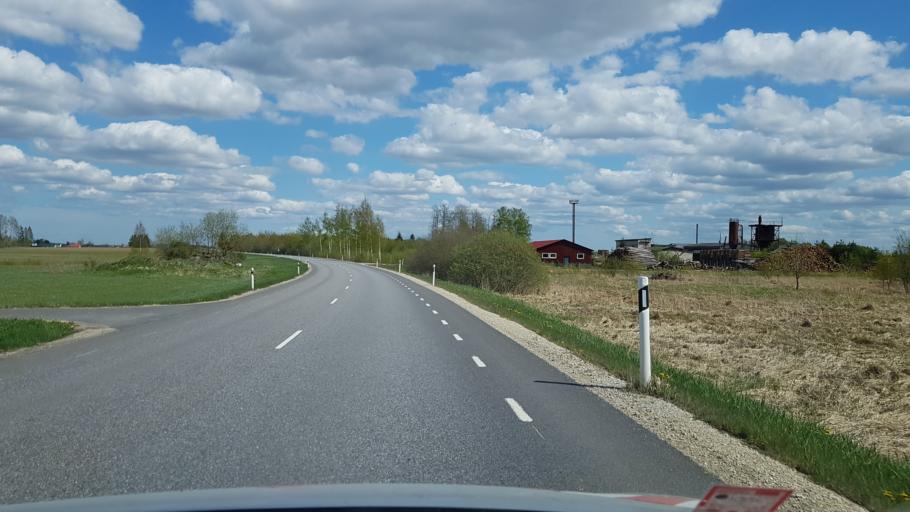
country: EE
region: Tartu
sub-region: UElenurme vald
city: Ulenurme
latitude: 58.3103
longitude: 26.6744
